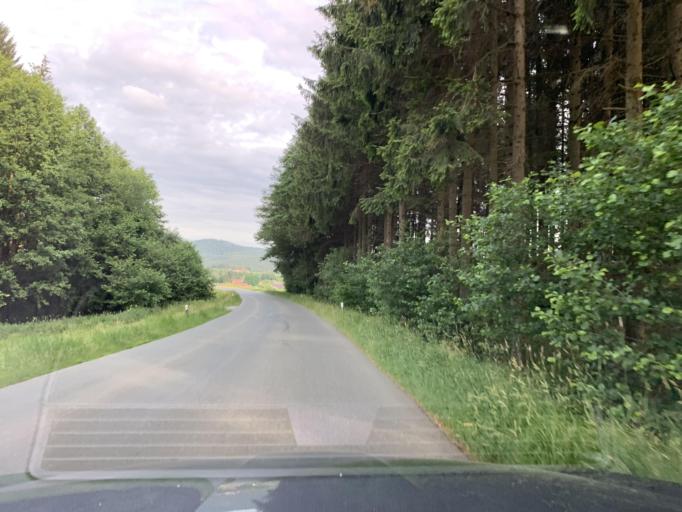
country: DE
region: Bavaria
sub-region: Upper Palatinate
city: Bach
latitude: 49.4062
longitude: 12.3819
